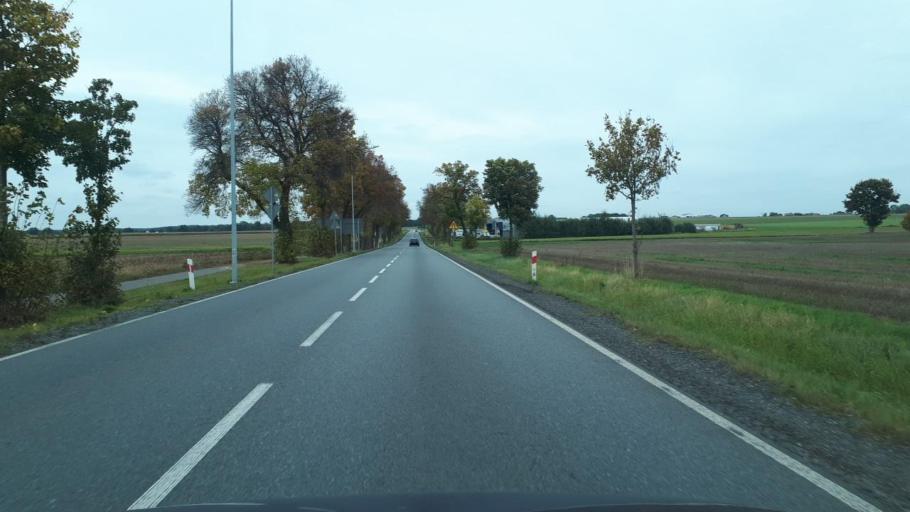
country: PL
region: Opole Voivodeship
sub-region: Powiat oleski
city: Dobrodzien
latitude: 50.7393
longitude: 18.4432
